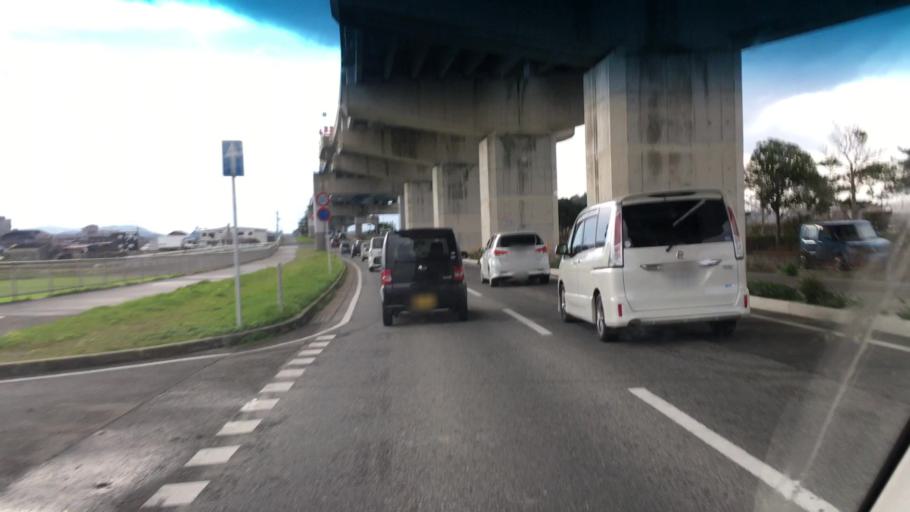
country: JP
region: Fukuoka
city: Maebaru-chuo
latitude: 33.5626
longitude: 130.2348
